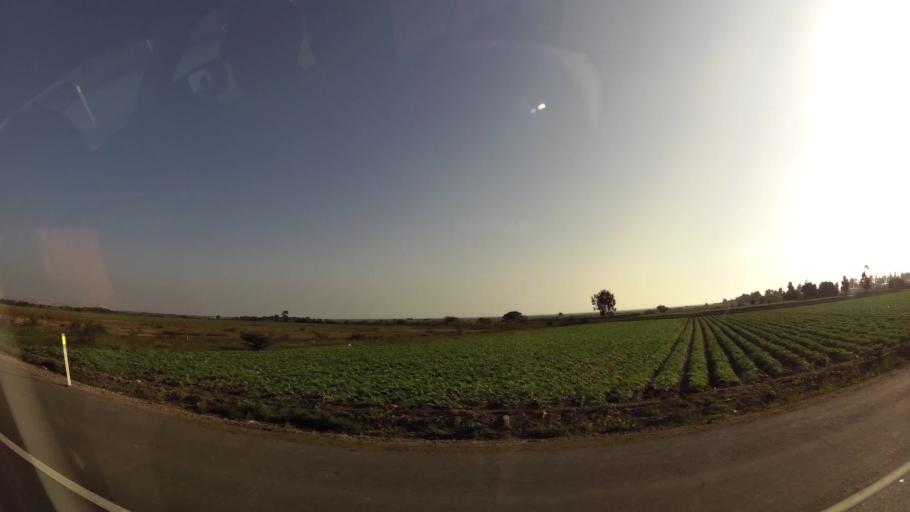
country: PE
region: Ica
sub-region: Provincia de Pisco
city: San Clemente
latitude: -13.5750
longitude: -76.1745
